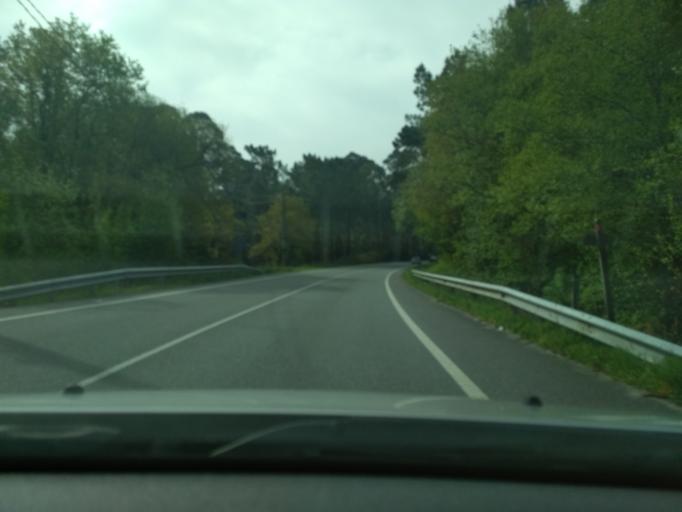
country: ES
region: Galicia
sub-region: Provincia de Pontevedra
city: Catoira
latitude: 42.6674
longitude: -8.7042
